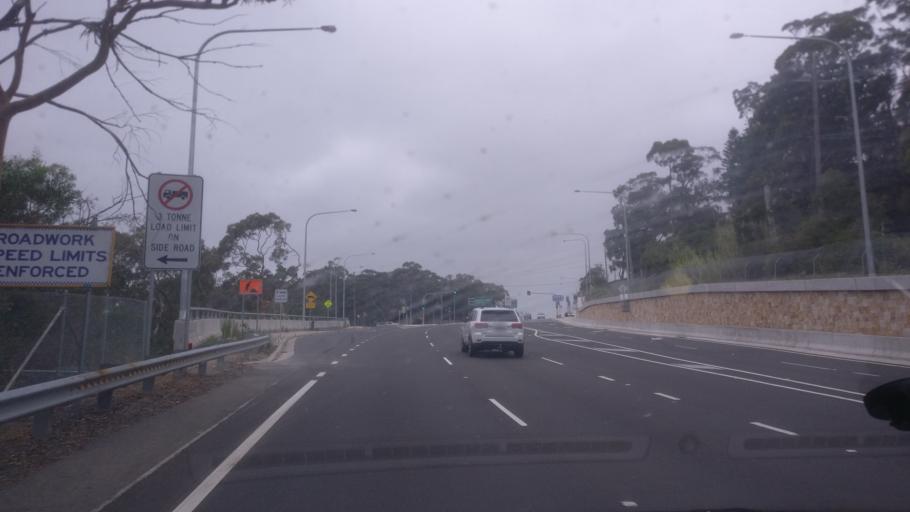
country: AU
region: New South Wales
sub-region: Warringah
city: Allambie Heights
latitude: -33.7485
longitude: 151.2349
